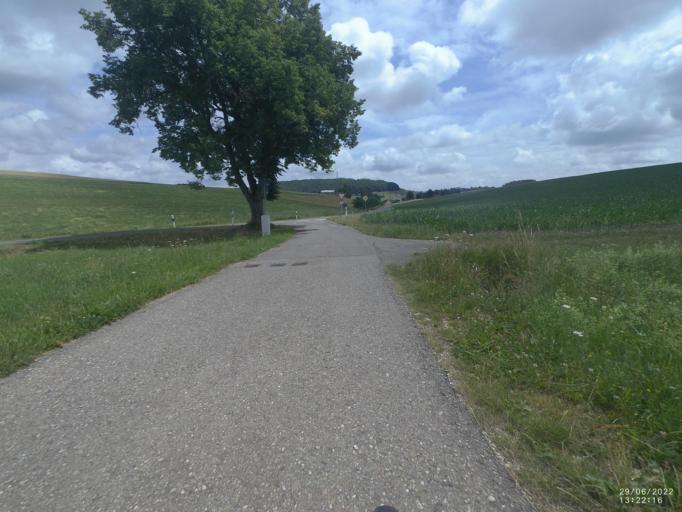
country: DE
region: Baden-Wuerttemberg
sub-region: Regierungsbezirk Stuttgart
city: Gerstetten
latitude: 48.6415
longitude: 9.9947
